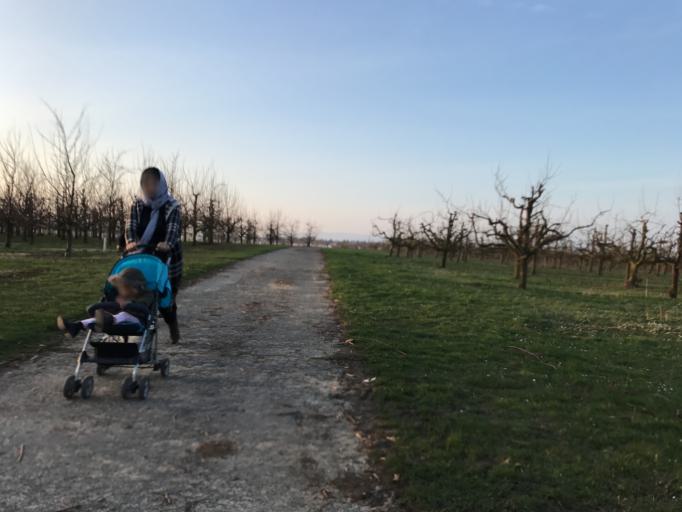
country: DE
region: Rheinland-Pfalz
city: Ober-Olm
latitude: 49.9627
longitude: 8.1974
